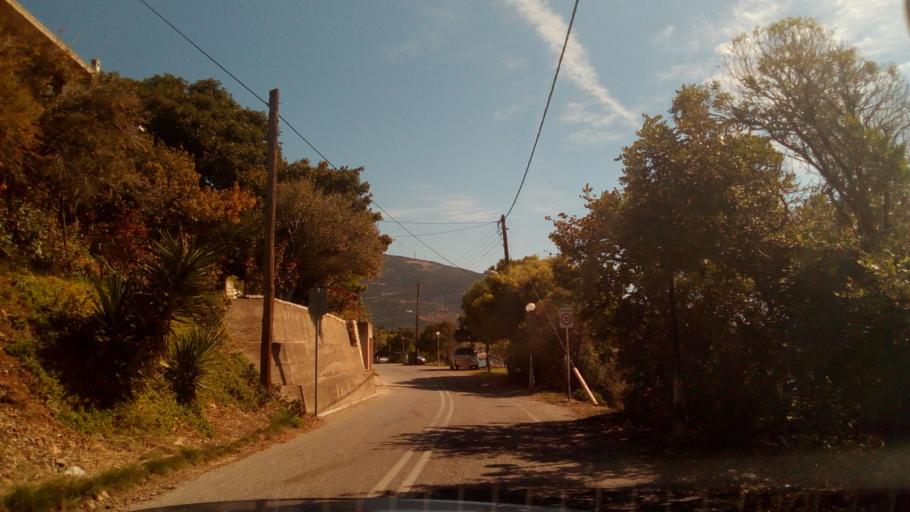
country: GR
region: West Greece
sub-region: Nomos Achaias
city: Selianitika
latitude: 38.3803
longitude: 22.0728
